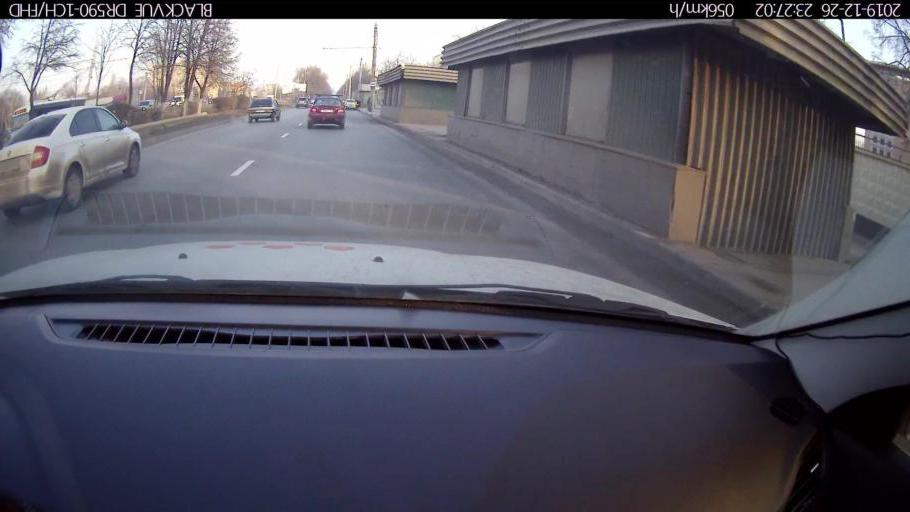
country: RU
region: Nizjnij Novgorod
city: Nizhniy Novgorod
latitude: 56.2519
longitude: 43.8897
